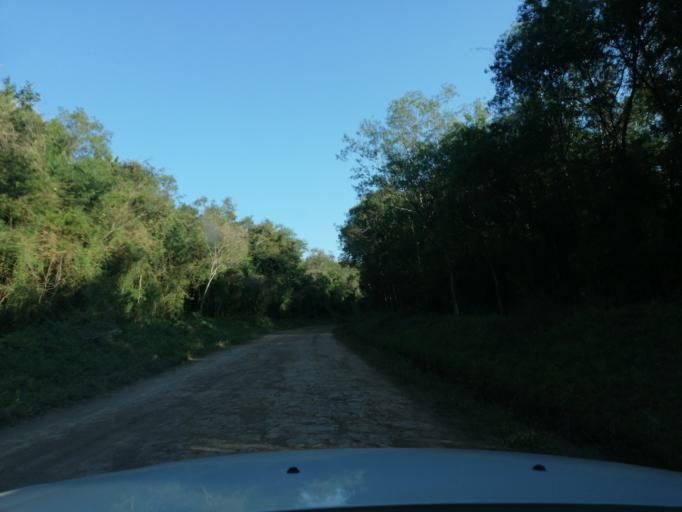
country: AR
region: Misiones
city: Cerro Cora
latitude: -27.6097
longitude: -55.7046
